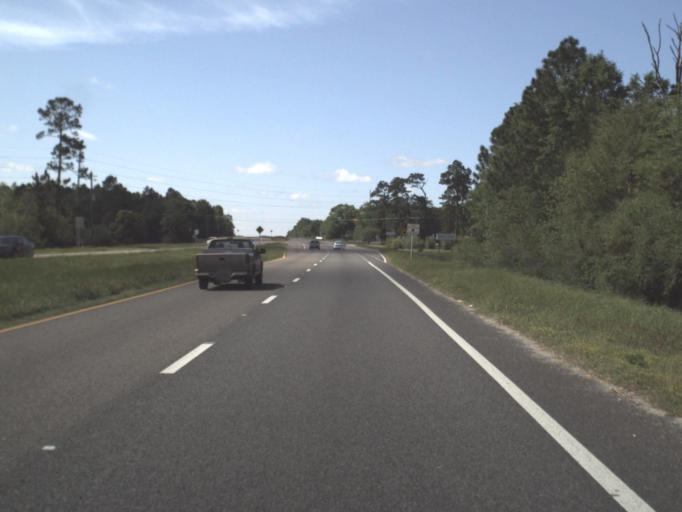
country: US
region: Florida
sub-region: Escambia County
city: Cantonment
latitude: 30.6270
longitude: -87.3301
